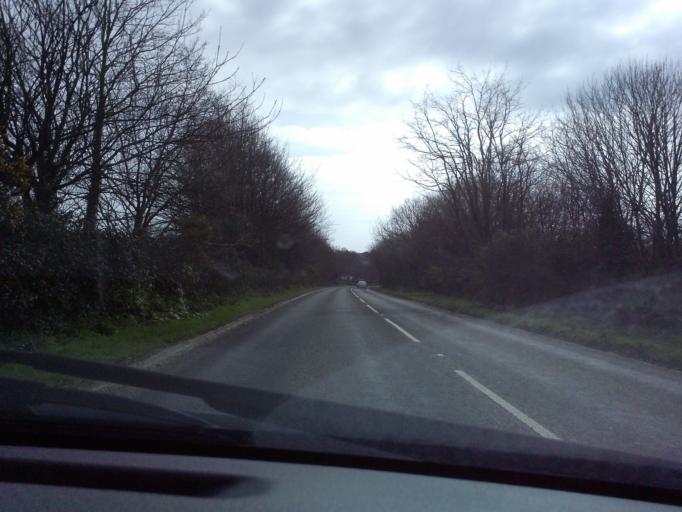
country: GB
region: England
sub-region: Cornwall
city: Penzance
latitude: 50.1205
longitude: -5.5512
